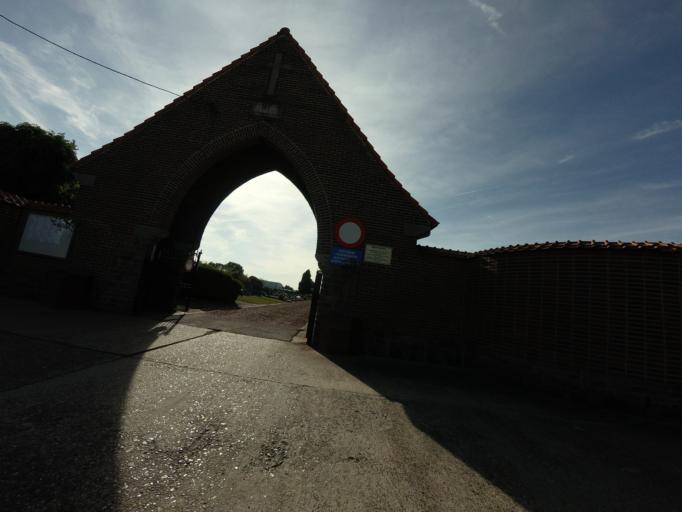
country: BE
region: Flanders
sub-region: Provincie Vlaams-Brabant
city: Kortenberg
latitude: 50.9079
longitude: 4.5617
